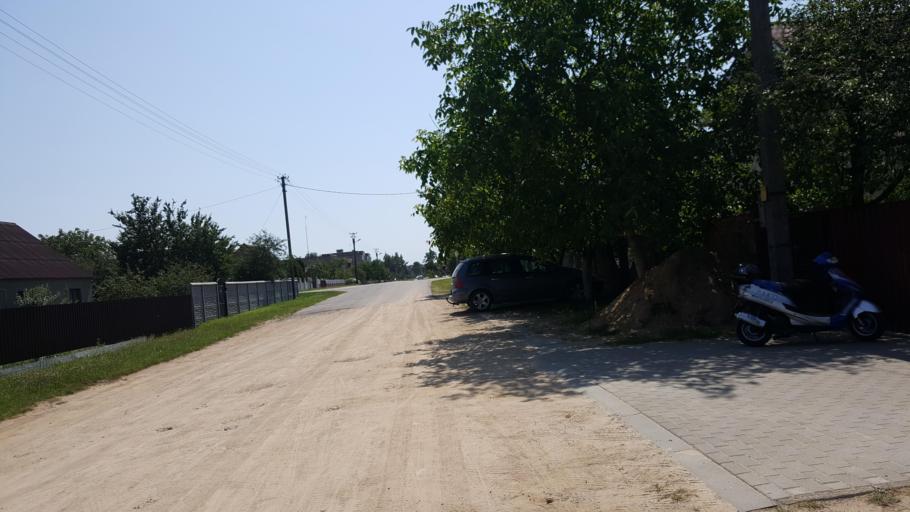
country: BY
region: Brest
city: Zhabinka
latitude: 52.1955
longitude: 23.9789
